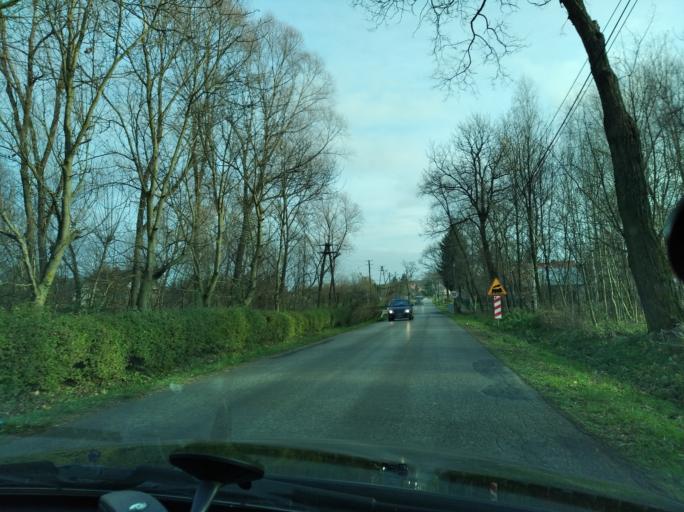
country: PL
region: Subcarpathian Voivodeship
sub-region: Powiat przeworski
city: Siedleczka
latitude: 49.9541
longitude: 22.3947
